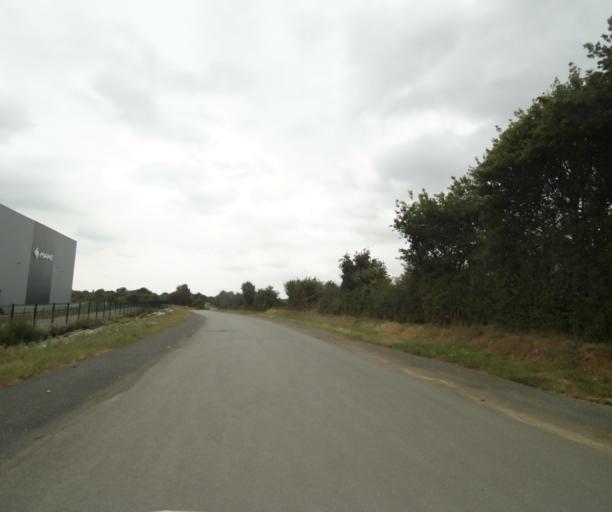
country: FR
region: Pays de la Loire
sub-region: Departement de la Sarthe
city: Solesmes
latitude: 47.8305
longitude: -0.2934
